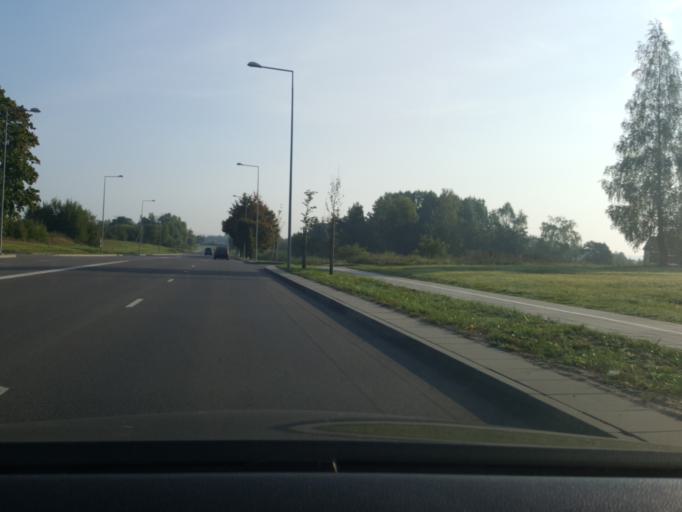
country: LT
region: Alytaus apskritis
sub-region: Alytus
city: Alytus
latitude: 54.4203
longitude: 24.0279
